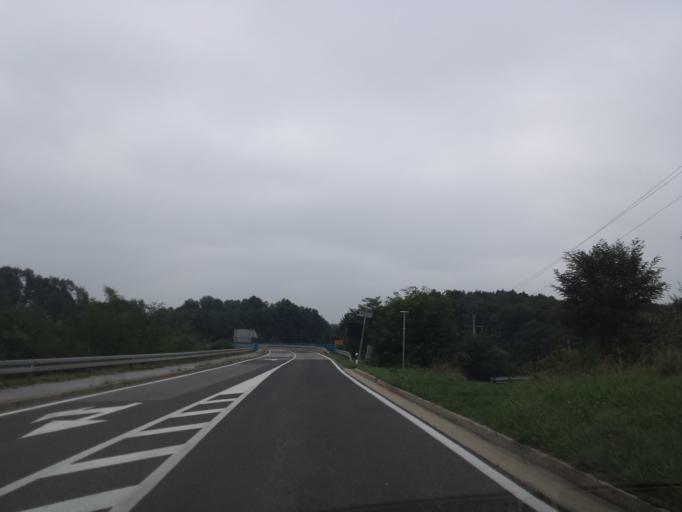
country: HR
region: Karlovacka
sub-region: Grad Karlovac
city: Karlovac
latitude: 45.4439
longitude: 15.4938
